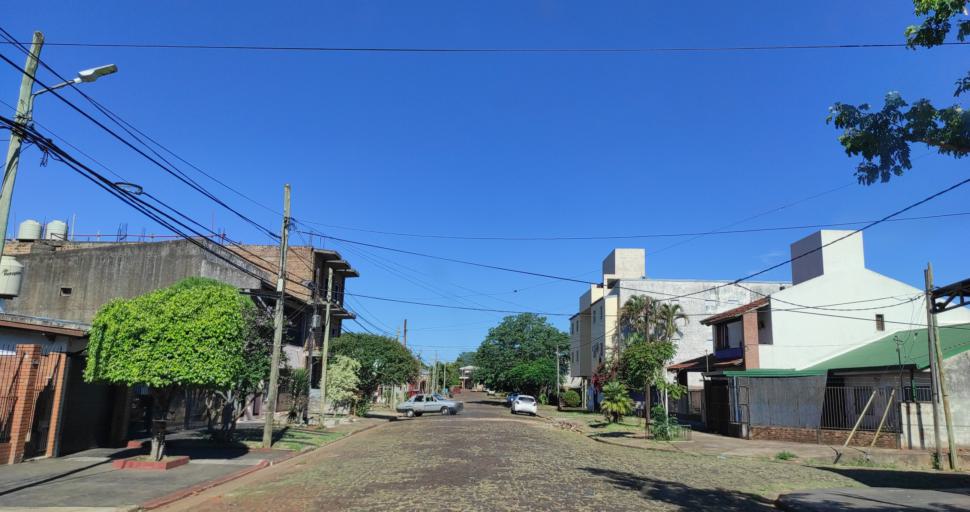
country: AR
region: Misiones
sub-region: Departamento de Capital
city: Posadas
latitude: -27.3887
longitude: -55.8989
